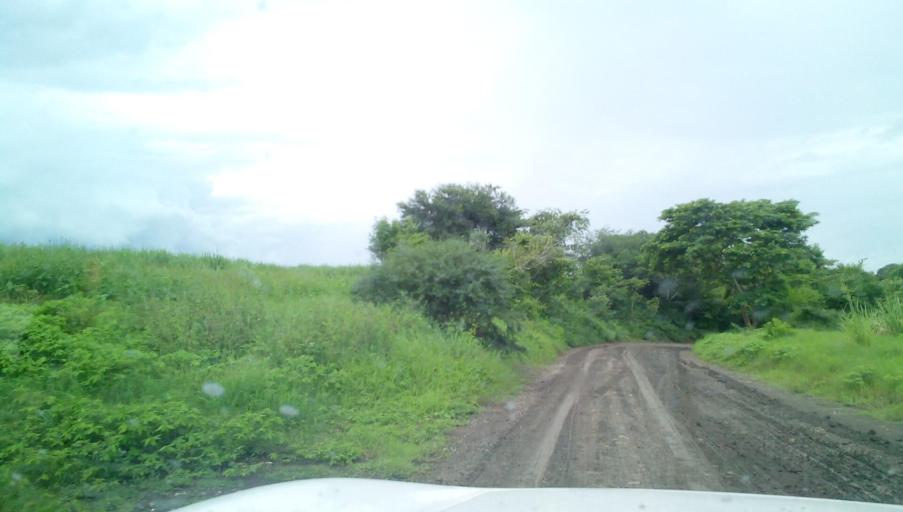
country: MX
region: Veracruz
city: Panuco
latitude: 21.8448
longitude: -98.1115
